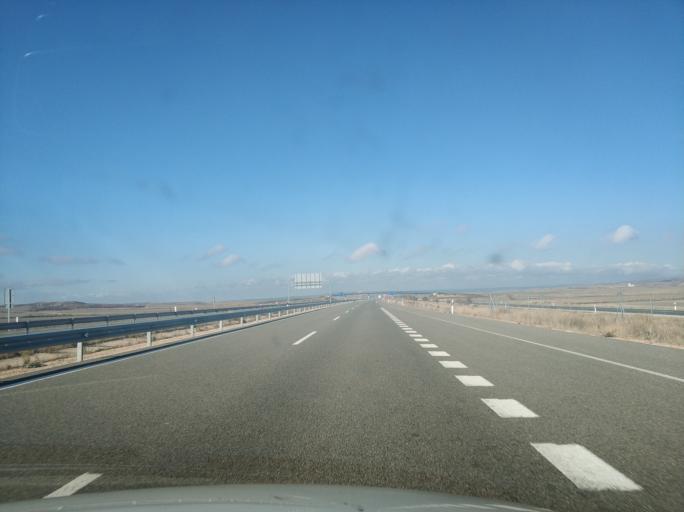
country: ES
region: Castille and Leon
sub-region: Provincia de Soria
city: Adradas
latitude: 41.3870
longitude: -2.4686
